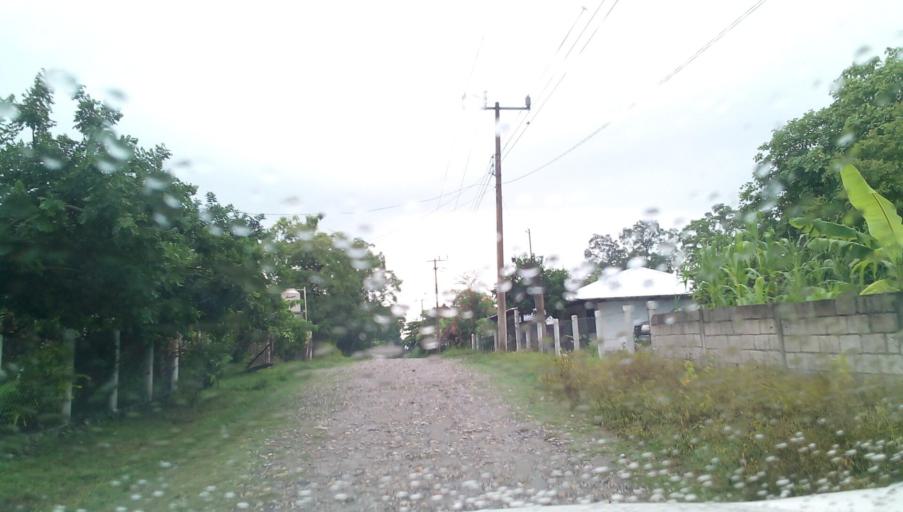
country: MX
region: Veracruz
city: Tempoal de Sanchez
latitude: 21.4157
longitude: -98.4256
